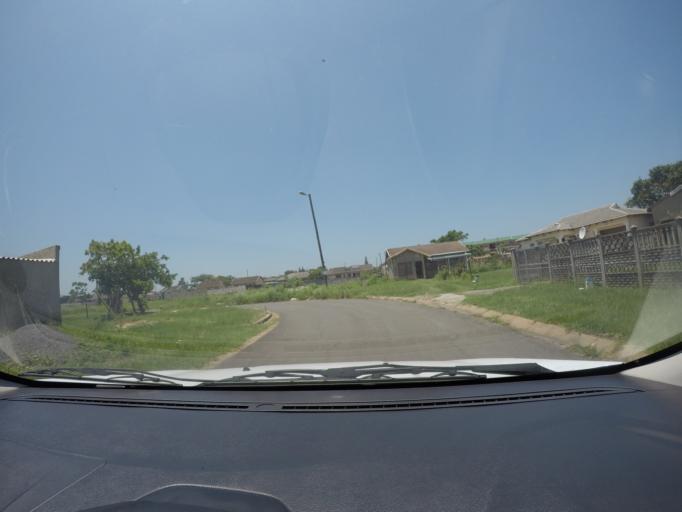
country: ZA
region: KwaZulu-Natal
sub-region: uThungulu District Municipality
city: eSikhawini
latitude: -28.8767
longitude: 31.8978
